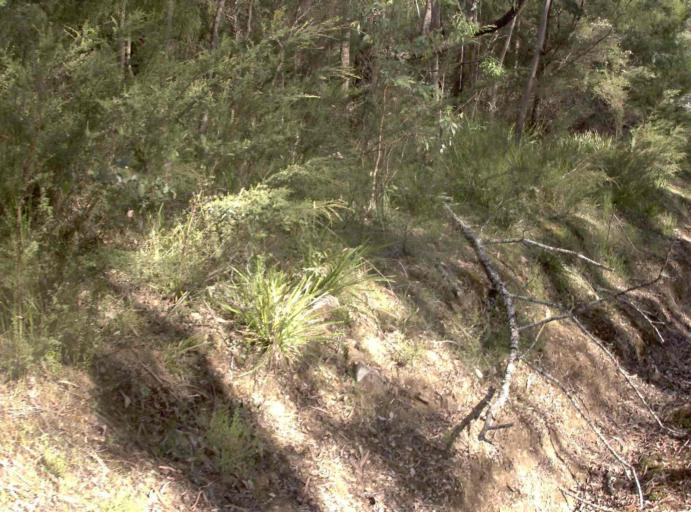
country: AU
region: Victoria
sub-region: East Gippsland
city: Lakes Entrance
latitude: -37.4789
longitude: 148.5566
